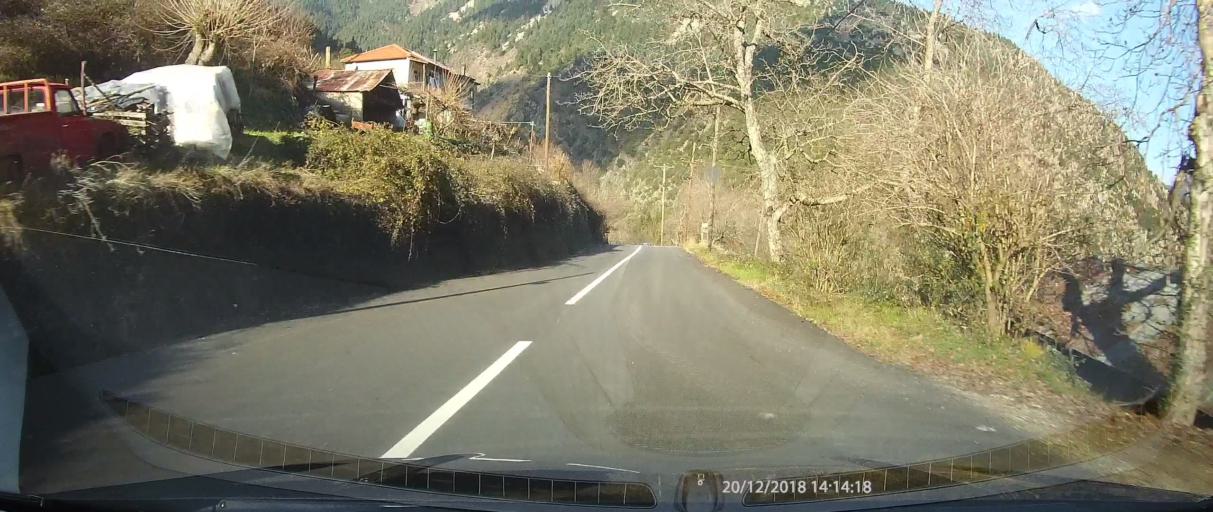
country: GR
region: West Greece
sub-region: Nomos Aitolias kai Akarnanias
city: Thermo
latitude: 38.7468
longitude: 21.6528
